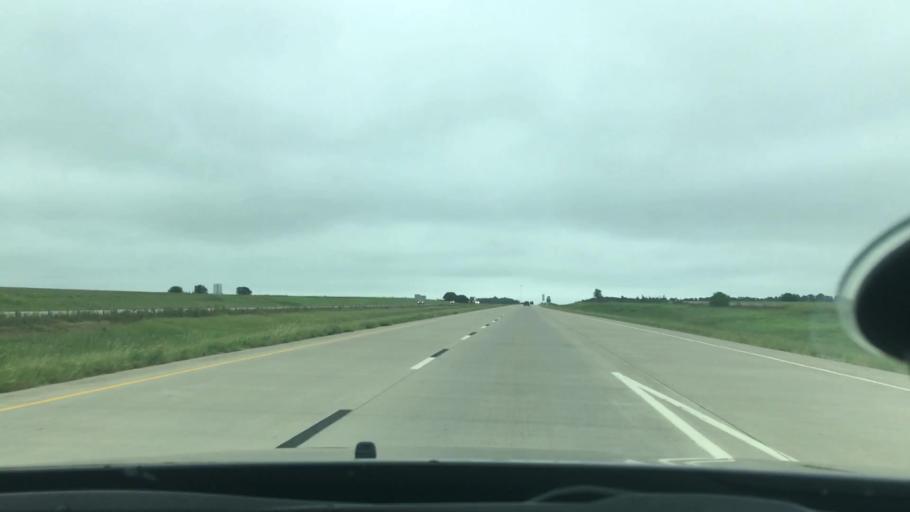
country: US
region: Oklahoma
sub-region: McIntosh County
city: Checotah
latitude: 35.4570
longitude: -95.4483
